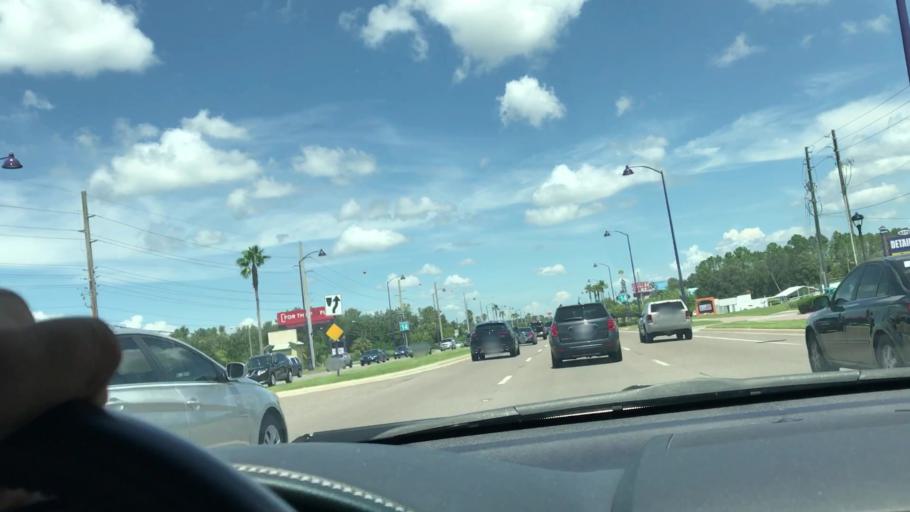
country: US
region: Florida
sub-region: Osceola County
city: Kissimmee
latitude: 28.3105
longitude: -81.4656
